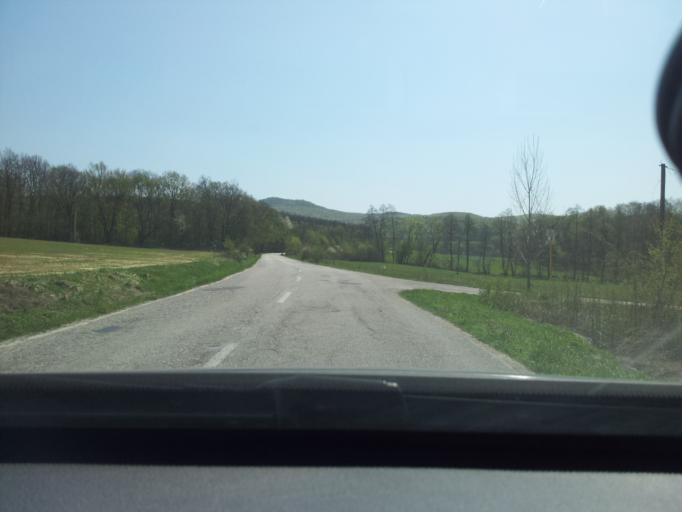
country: SK
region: Nitriansky
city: Partizanske
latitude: 48.5329
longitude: 18.3612
